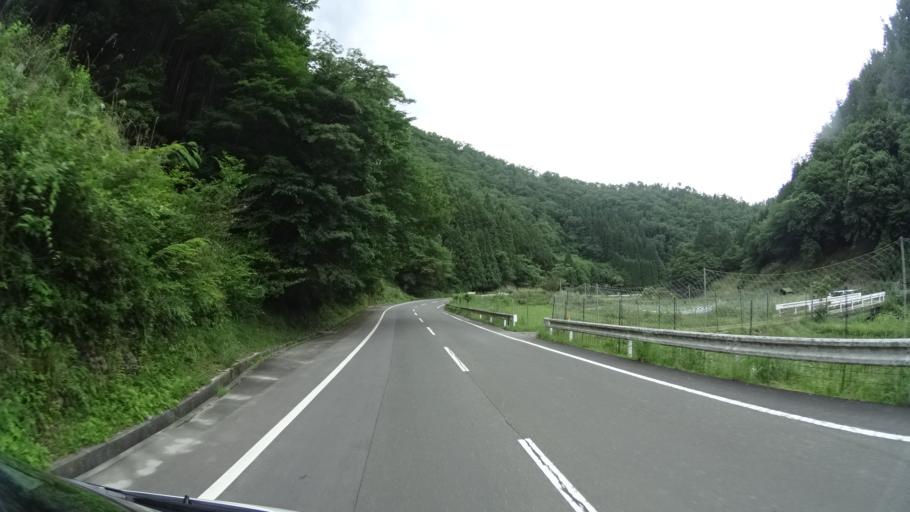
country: JP
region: Hyogo
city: Sasayama
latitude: 35.0611
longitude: 135.3923
